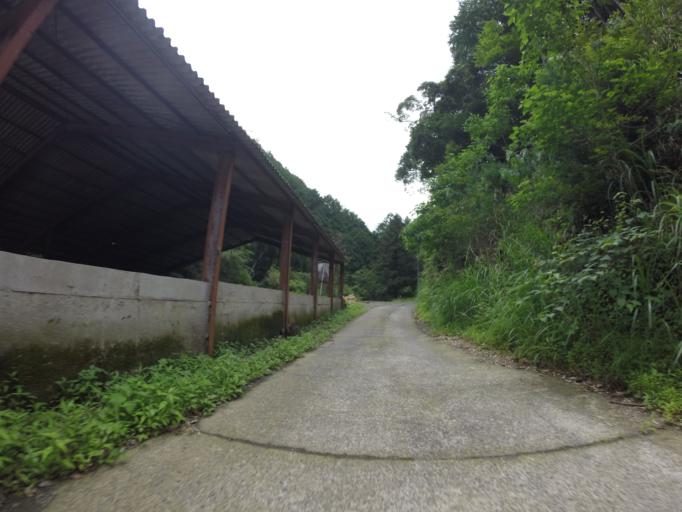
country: JP
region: Shizuoka
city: Shizuoka-shi
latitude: 35.0240
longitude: 138.3048
